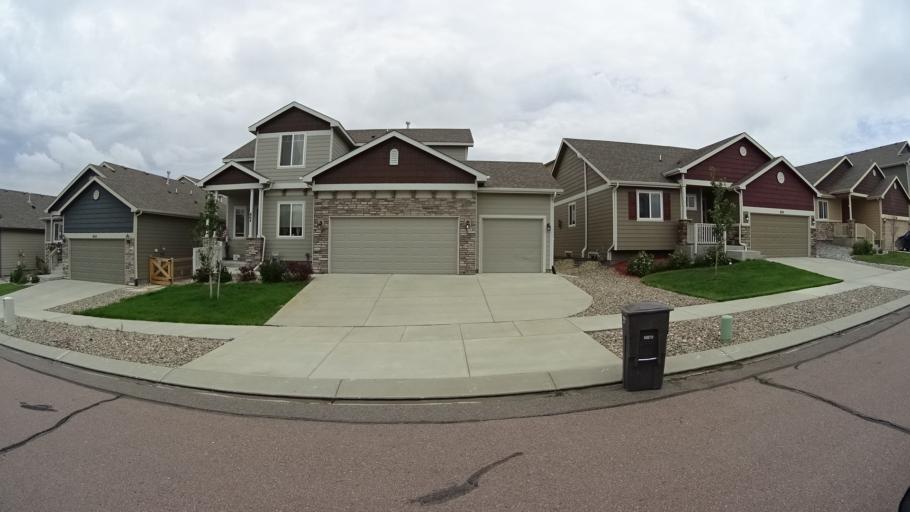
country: US
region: Colorado
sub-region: El Paso County
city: Gleneagle
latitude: 39.0107
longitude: -104.8117
